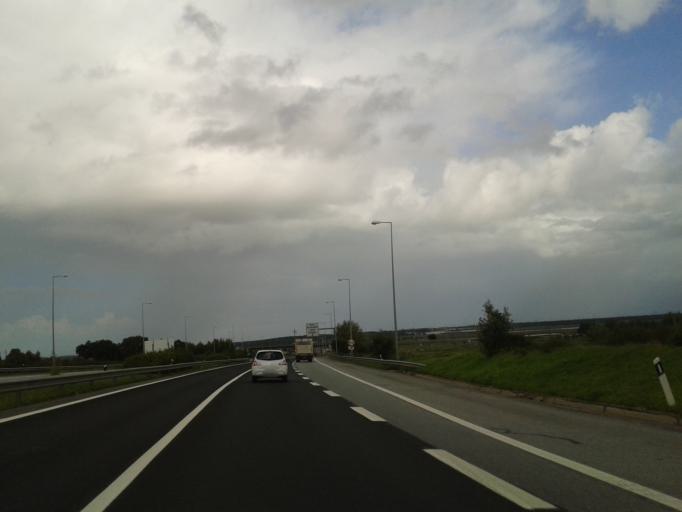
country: PT
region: Setubal
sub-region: Alcochete
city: Alcochete
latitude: 38.7387
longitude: -8.9331
